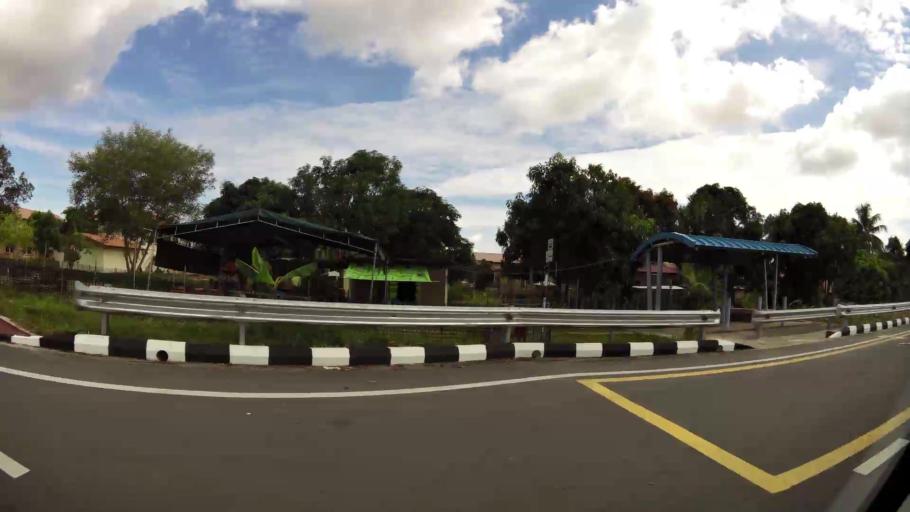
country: BN
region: Brunei and Muara
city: Bandar Seri Begawan
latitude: 4.9366
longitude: 114.8995
